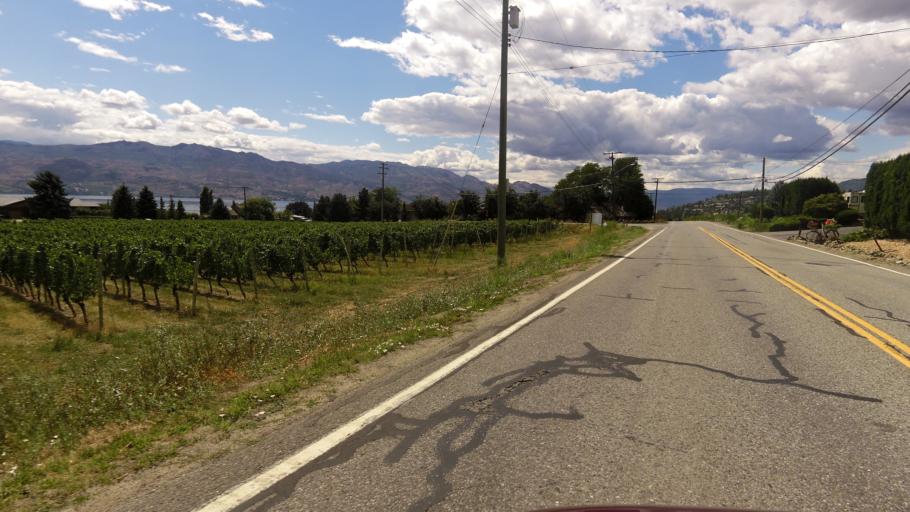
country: CA
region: British Columbia
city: West Kelowna
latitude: 49.8442
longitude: -119.5648
